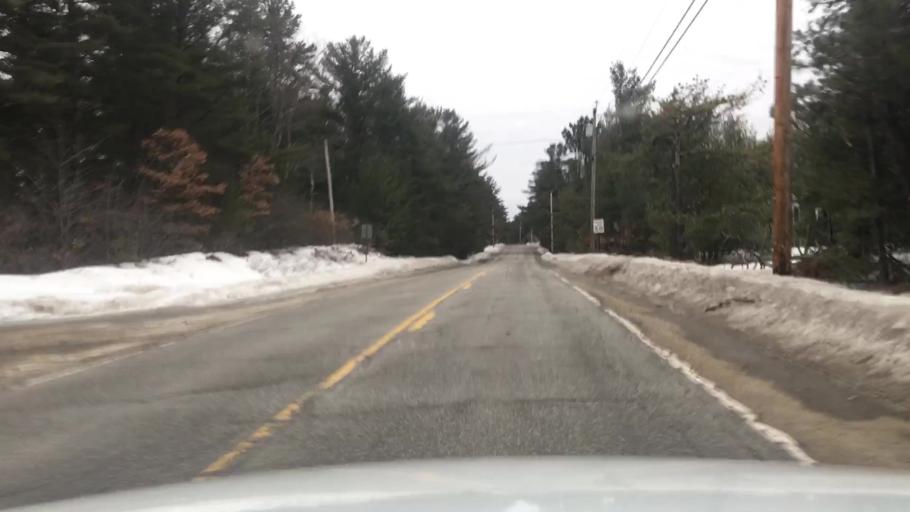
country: US
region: Maine
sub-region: York County
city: Shapleigh
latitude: 43.5633
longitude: -70.8579
